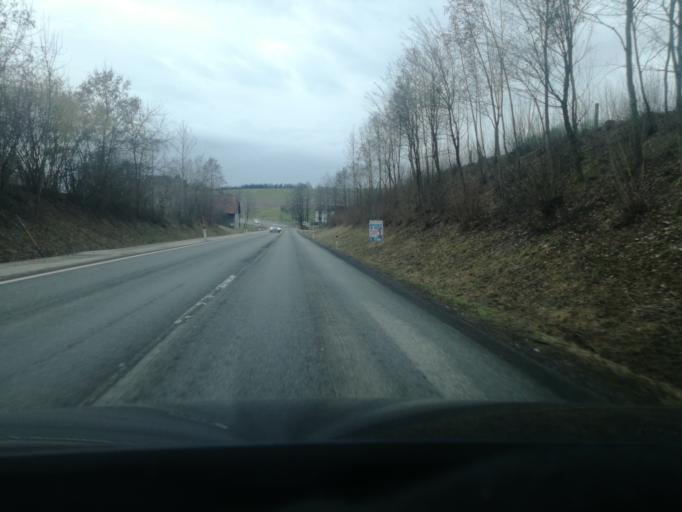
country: AT
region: Upper Austria
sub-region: Politischer Bezirk Vocklabruck
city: Frankenburg
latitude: 48.0543
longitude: 13.4823
